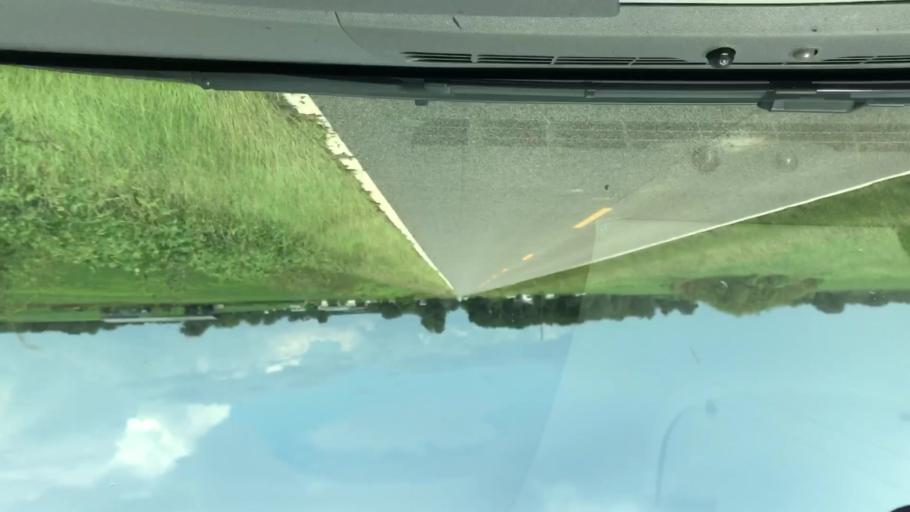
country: US
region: Georgia
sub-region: Seminole County
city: Donalsonville
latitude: 31.1119
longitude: -84.9958
